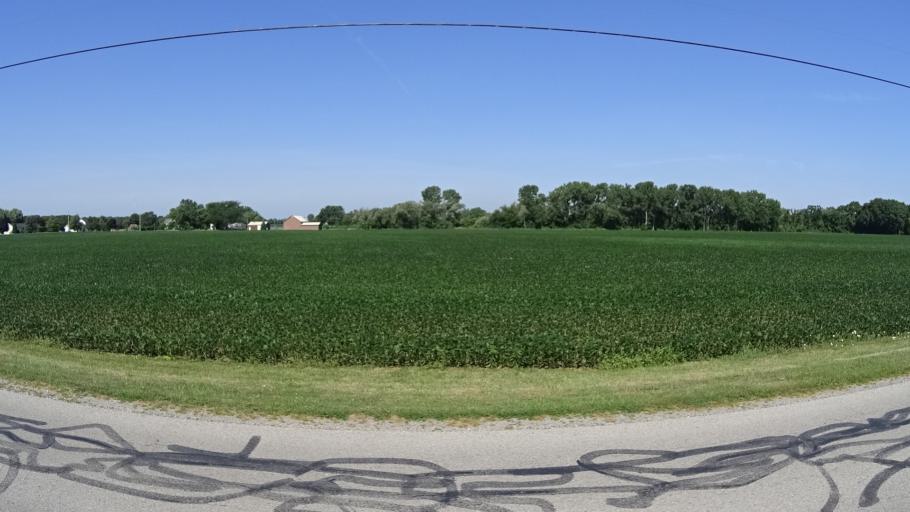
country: US
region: Ohio
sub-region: Huron County
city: Bellevue
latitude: 41.3634
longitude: -82.7865
